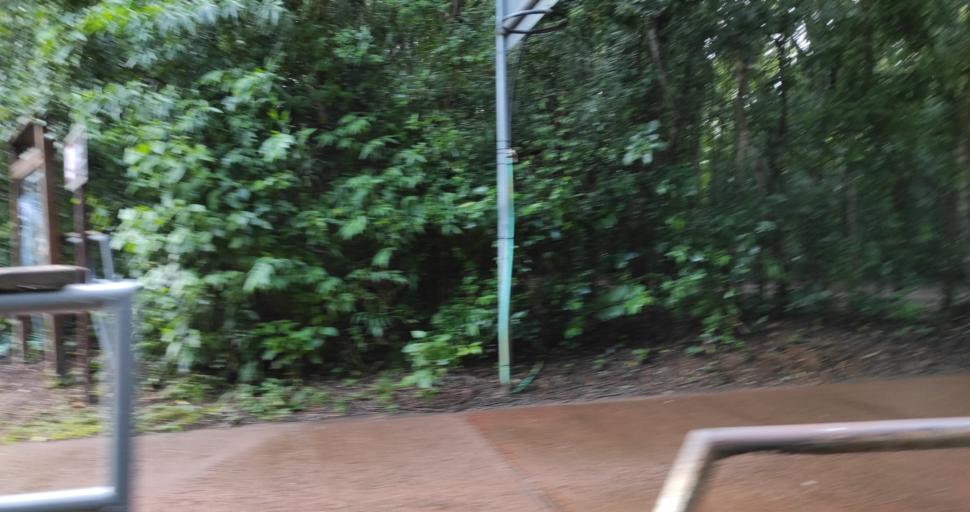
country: AR
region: Misiones
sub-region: Departamento de Iguazu
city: Puerto Iguazu
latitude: -25.6841
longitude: -54.4488
